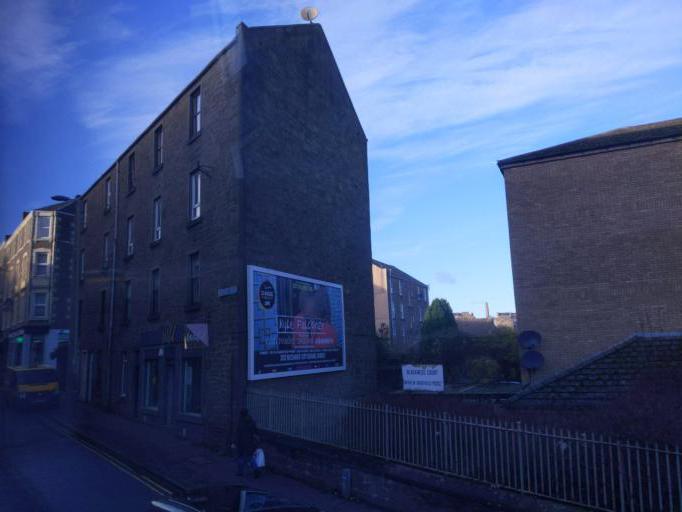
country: GB
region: Scotland
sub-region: Dundee City
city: Dundee
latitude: 56.4602
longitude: -2.9927
